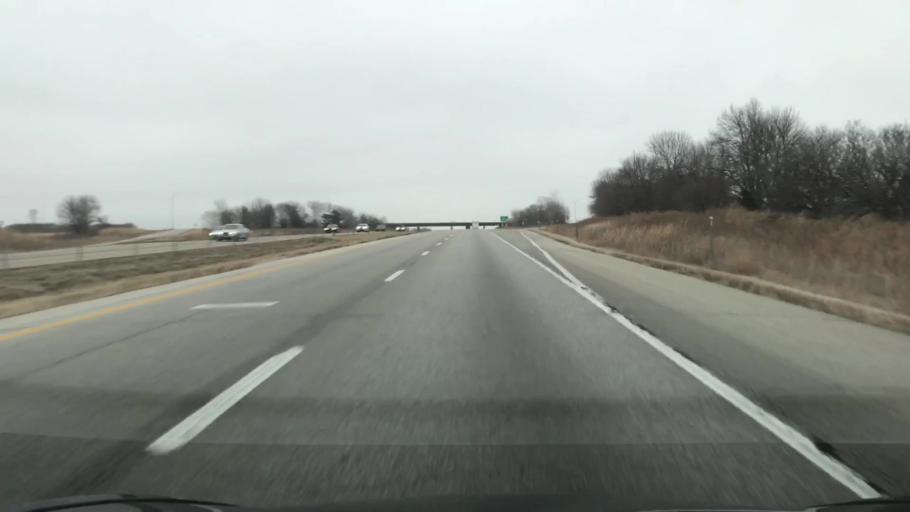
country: US
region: Iowa
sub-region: Madison County
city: Earlham
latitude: 41.5187
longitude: -94.0831
